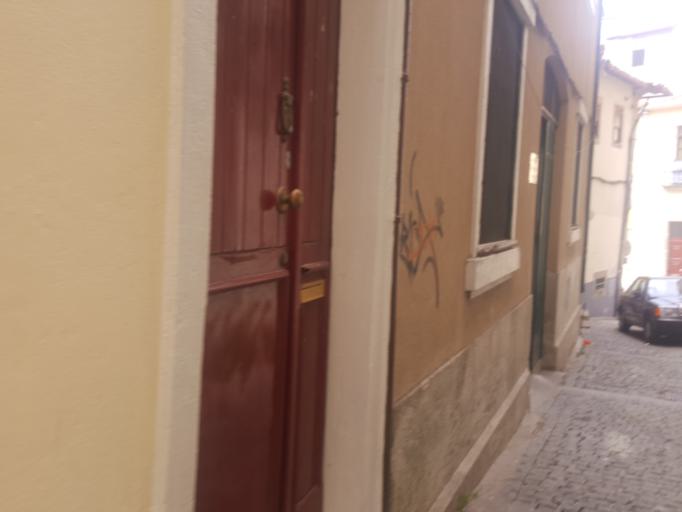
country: PT
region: Porto
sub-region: Porto
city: Porto
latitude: 41.1437
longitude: -8.6172
